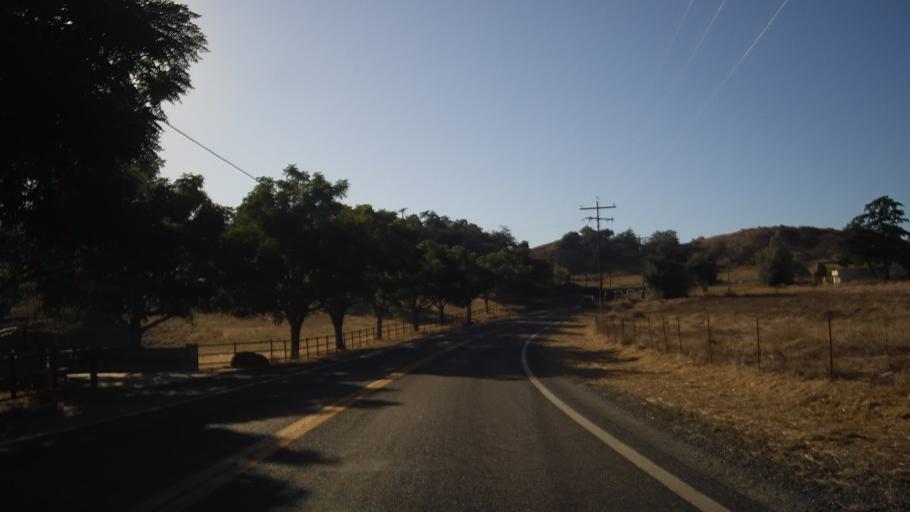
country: US
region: California
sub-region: San Diego County
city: San Diego Country Estates
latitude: 33.0647
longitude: -116.7579
